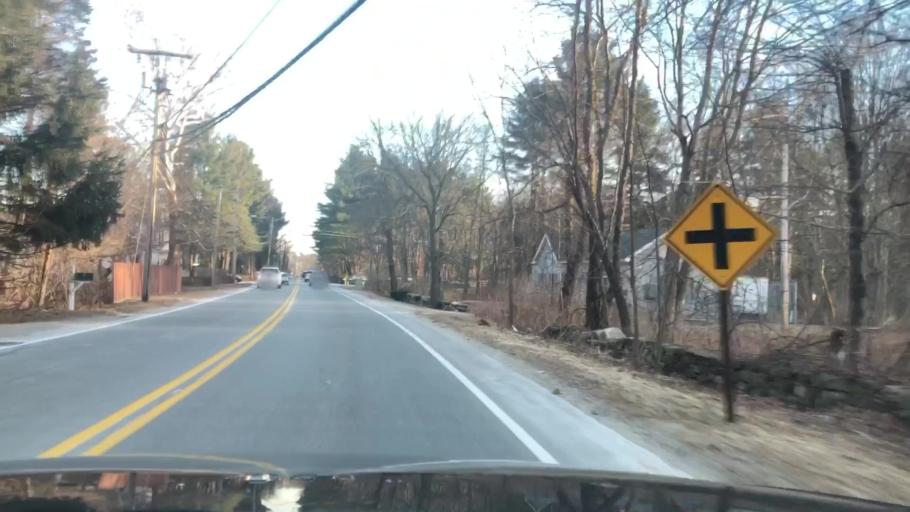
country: US
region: Massachusetts
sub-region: Worcester County
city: Bolton
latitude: 42.4367
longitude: -71.6153
